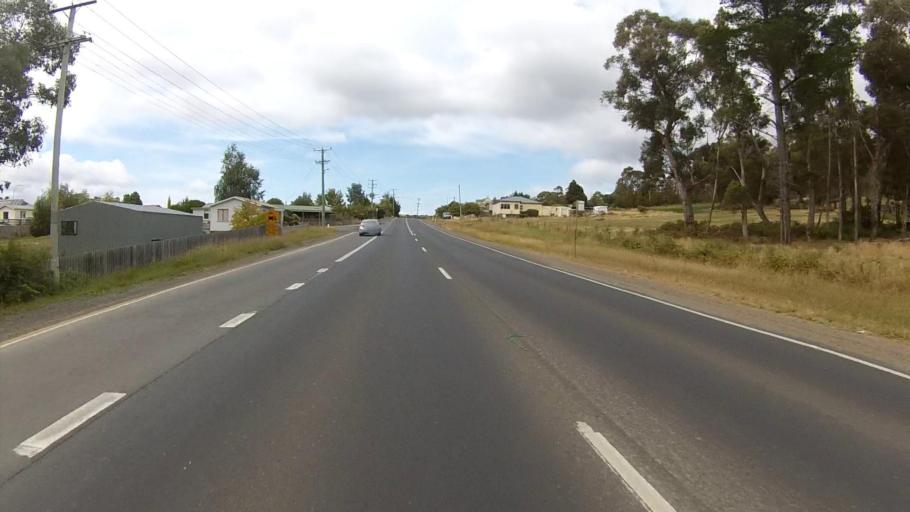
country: AU
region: Tasmania
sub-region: Kingborough
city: Margate
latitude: -43.0510
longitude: 147.2625
